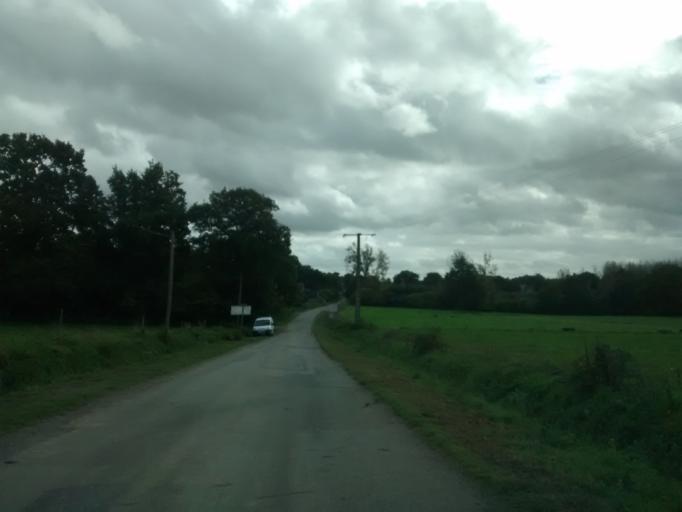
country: FR
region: Brittany
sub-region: Departement d'Ille-et-Vilaine
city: Chateaubourg
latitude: 48.1293
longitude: -1.4204
